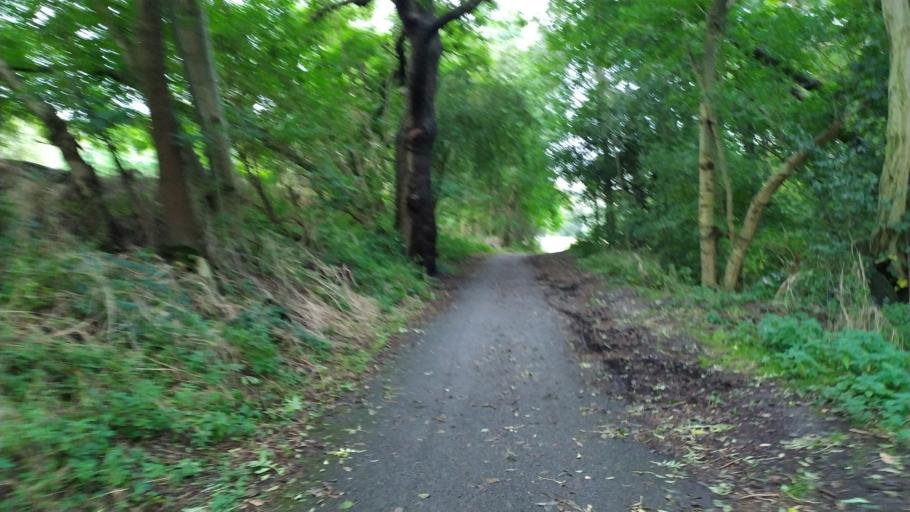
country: GB
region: England
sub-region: City and Borough of Leeds
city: Chapel Allerton
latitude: 53.8192
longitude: -1.5502
